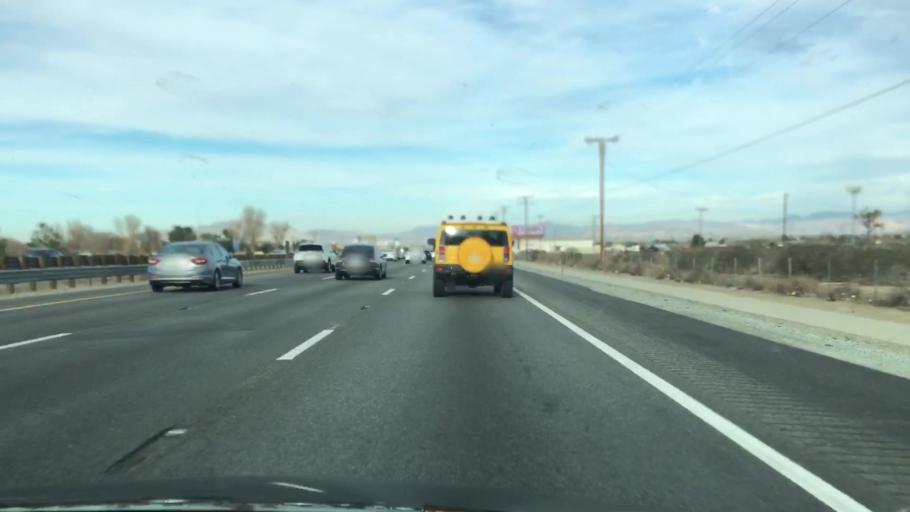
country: US
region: California
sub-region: San Bernardino County
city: Mountain View Acres
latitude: 34.4564
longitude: -117.3564
